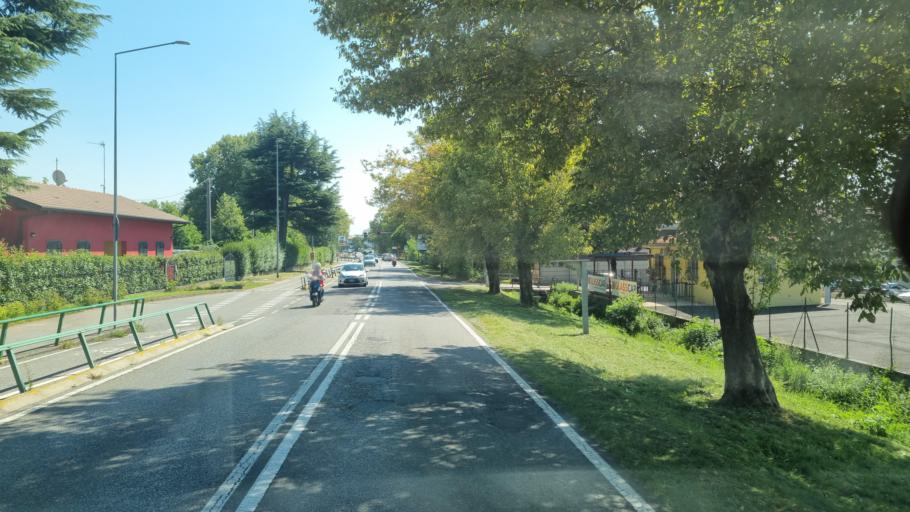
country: IT
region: Lombardy
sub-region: Provincia di Bergamo
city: Azzano San Paolo
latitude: 45.6671
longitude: 9.6762
